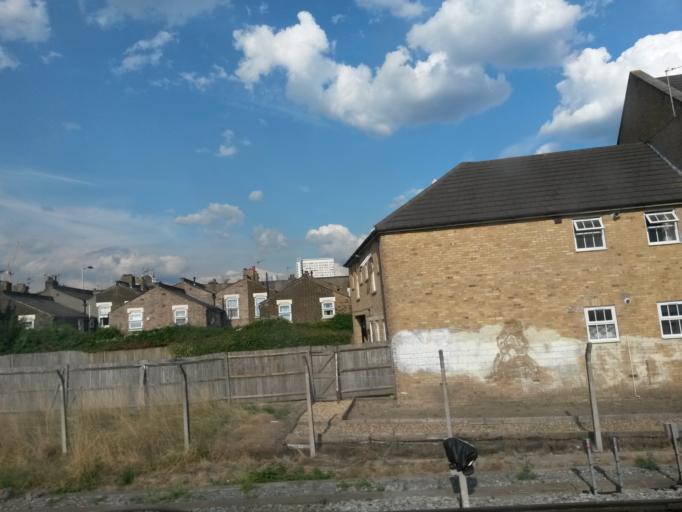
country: GB
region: England
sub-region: Greater London
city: Poplar
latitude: 51.4868
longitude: -0.0439
